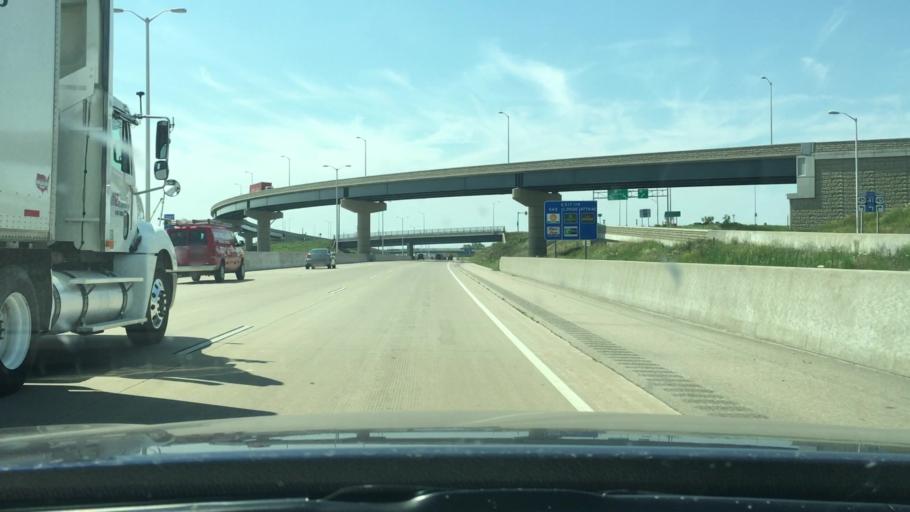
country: US
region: Wisconsin
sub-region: Winnebago County
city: Oshkosh
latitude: 44.0625
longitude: -88.5724
